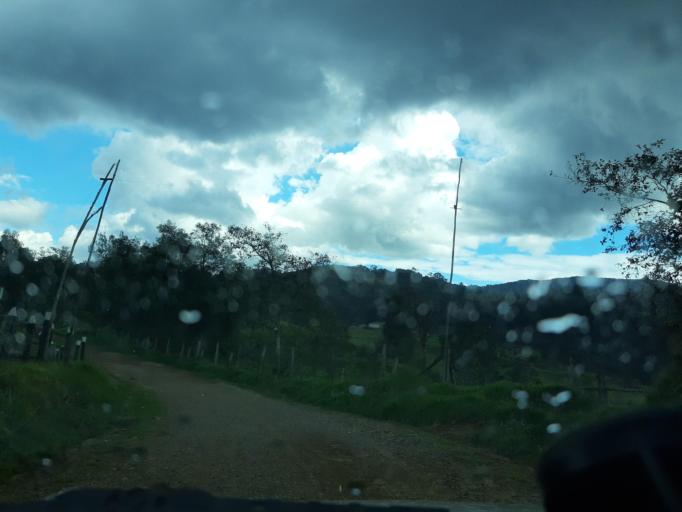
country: CO
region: Boyaca
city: Raquira
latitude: 5.4913
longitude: -73.6994
